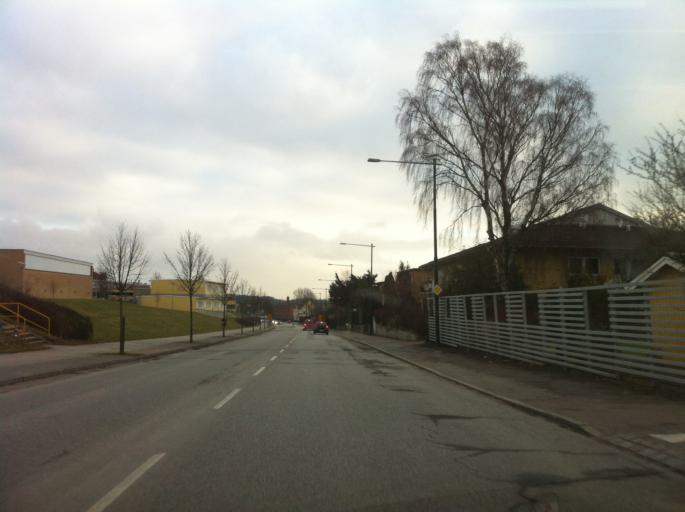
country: SE
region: Skane
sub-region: Kavlinge Kommun
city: Kaevlinge
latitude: 55.7938
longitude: 13.1003
